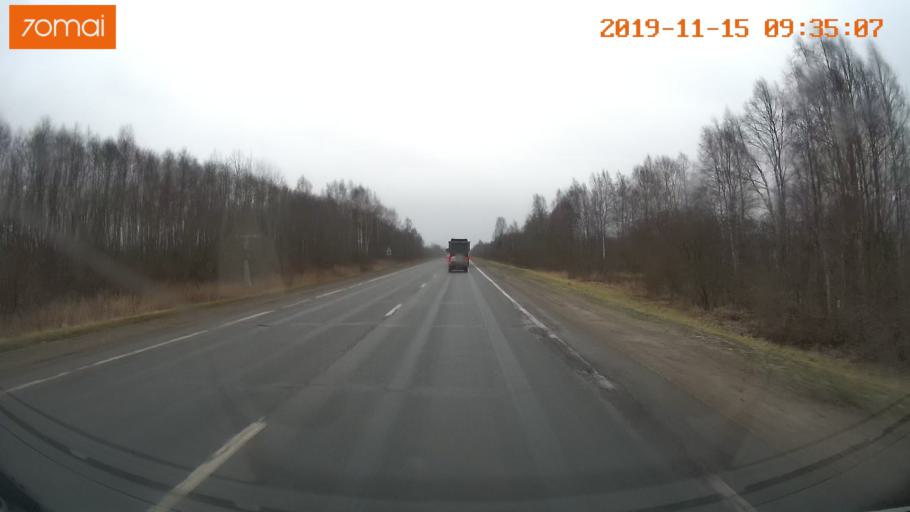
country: RU
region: Vologda
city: Sheksna
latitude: 59.2561
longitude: 38.3930
